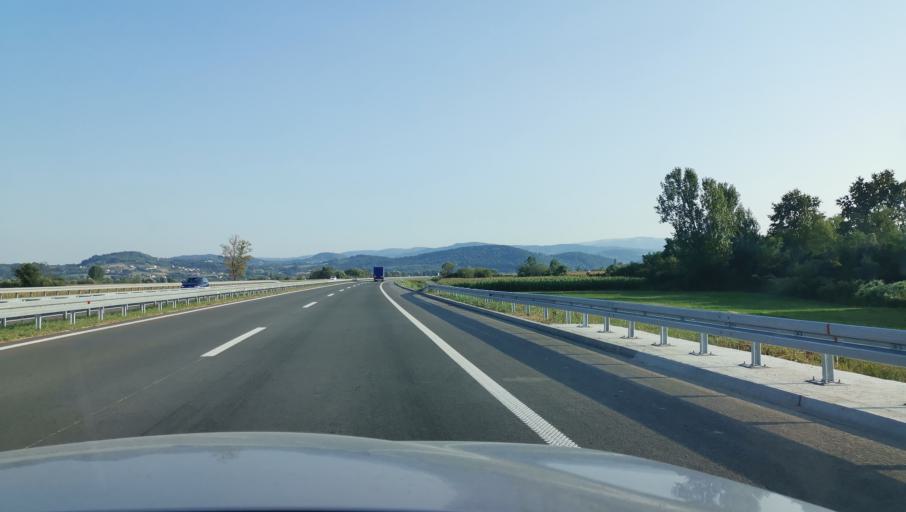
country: RS
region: Central Serbia
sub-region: Kolubarski Okrug
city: Ljig
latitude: 44.2630
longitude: 20.2707
